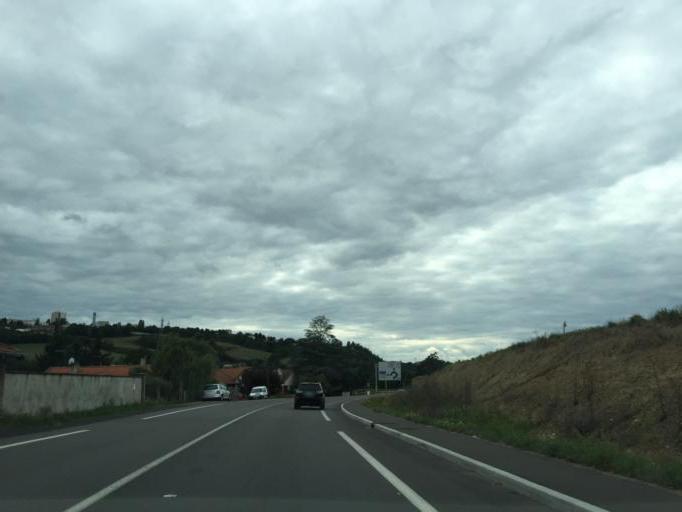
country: FR
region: Rhone-Alpes
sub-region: Departement de la Loire
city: La Talaudiere
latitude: 45.4771
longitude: 4.4157
